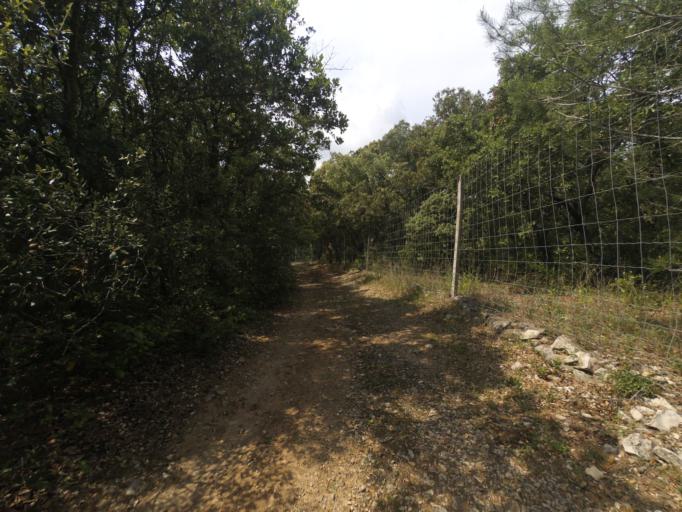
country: FR
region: Languedoc-Roussillon
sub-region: Departement du Gard
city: Vergeze
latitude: 43.7536
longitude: 4.2146
